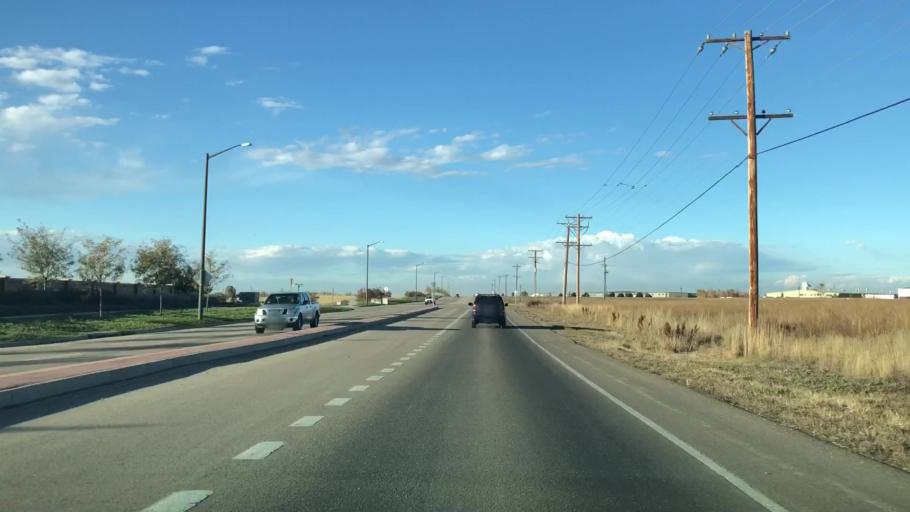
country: US
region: Colorado
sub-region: Larimer County
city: Loveland
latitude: 40.4347
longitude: -105.0204
